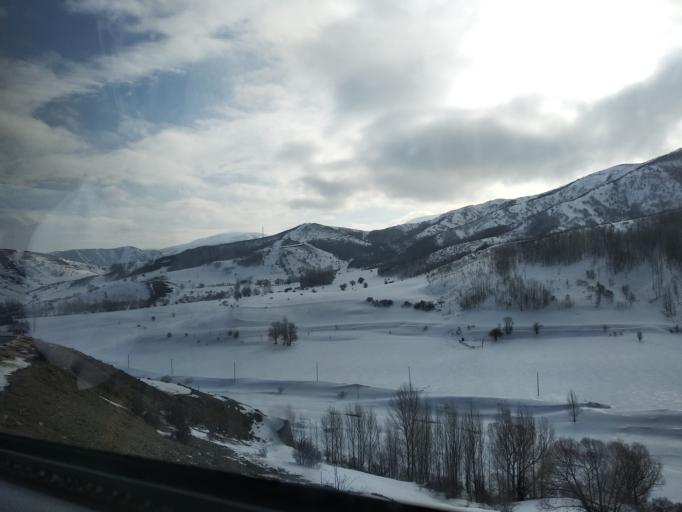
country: TR
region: Erzincan
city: Catalarmut
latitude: 39.8999
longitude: 39.3969
